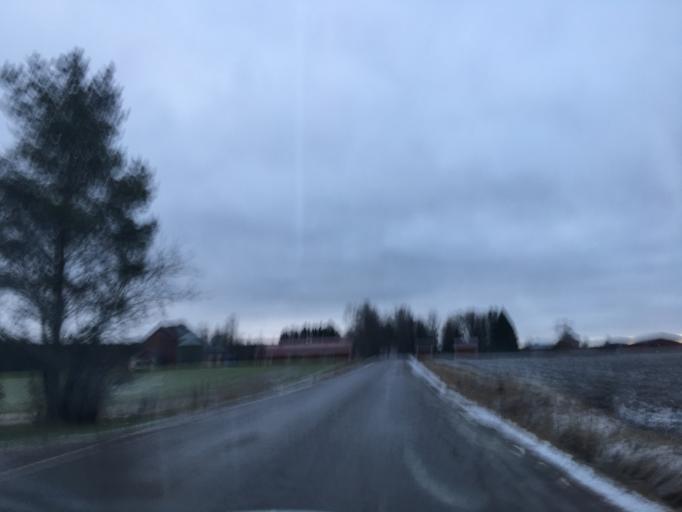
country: FI
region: Varsinais-Suomi
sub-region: Loimaa
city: Aura
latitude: 60.6277
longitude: 22.5841
